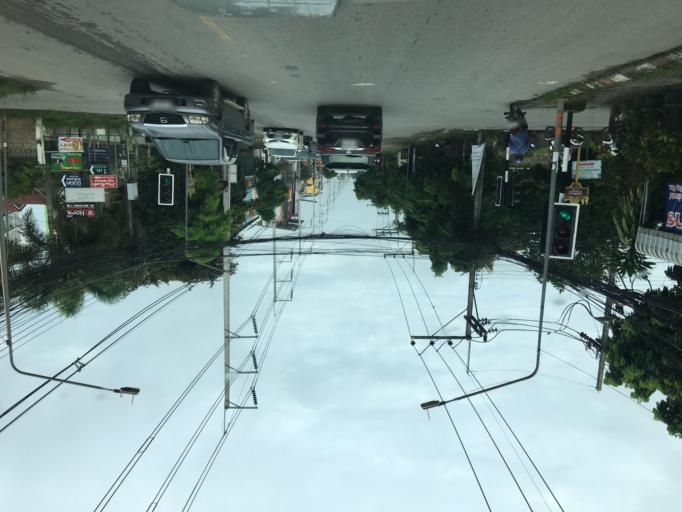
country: TH
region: Chiang Rai
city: Chiang Rai
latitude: 19.9016
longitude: 99.8141
